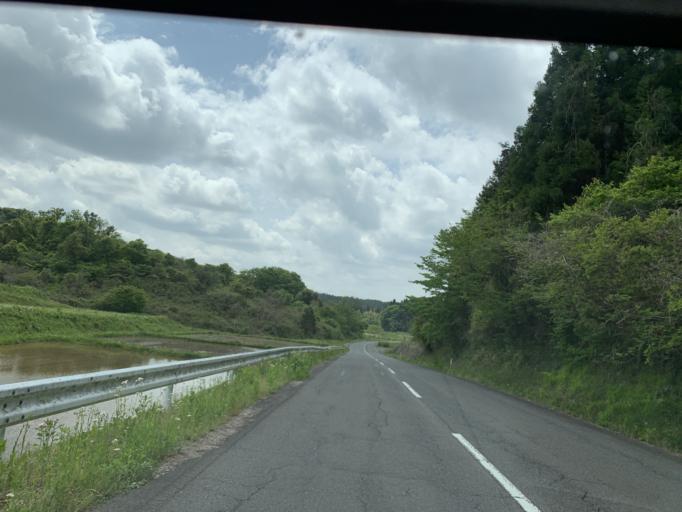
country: JP
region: Miyagi
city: Furukawa
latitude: 38.7097
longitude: 140.9180
